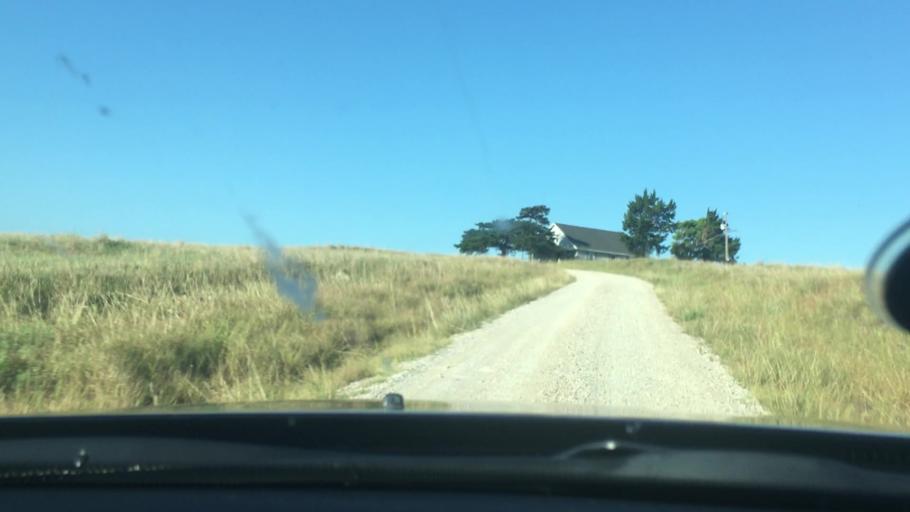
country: US
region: Oklahoma
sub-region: Johnston County
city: Tishomingo
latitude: 34.4155
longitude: -96.7621
